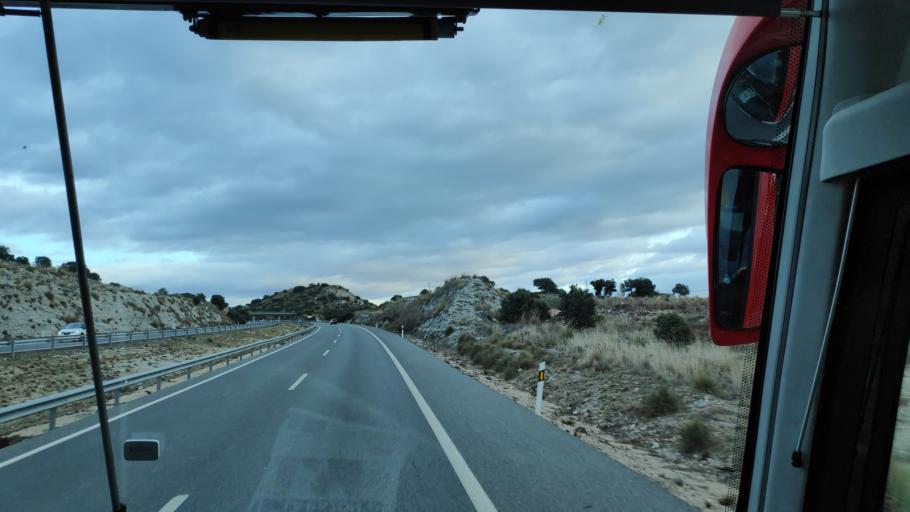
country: ES
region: Madrid
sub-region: Provincia de Madrid
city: Fuentiduena de Tajo
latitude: 40.1437
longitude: -3.2130
